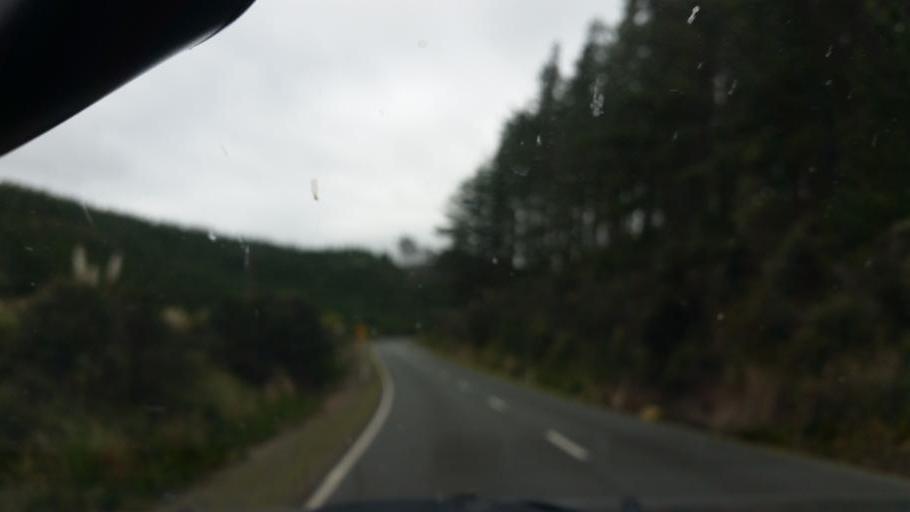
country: NZ
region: Northland
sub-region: Kaipara District
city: Dargaville
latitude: -35.8203
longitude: 173.7106
